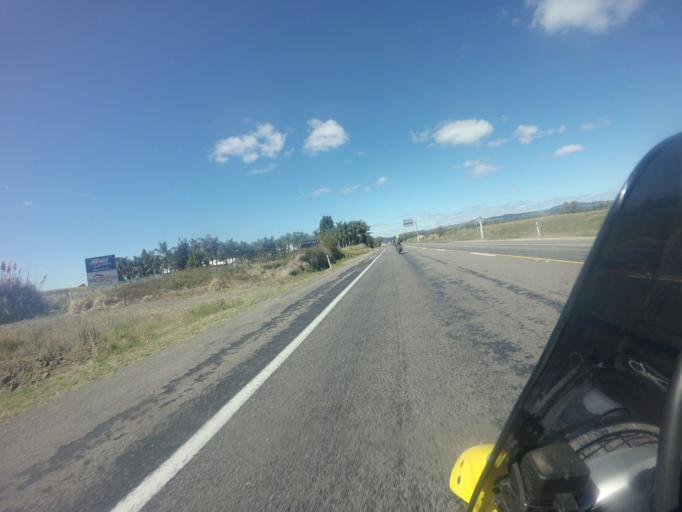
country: NZ
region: Bay of Plenty
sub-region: Whakatane District
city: Whakatane
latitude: -37.9489
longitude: 176.9395
